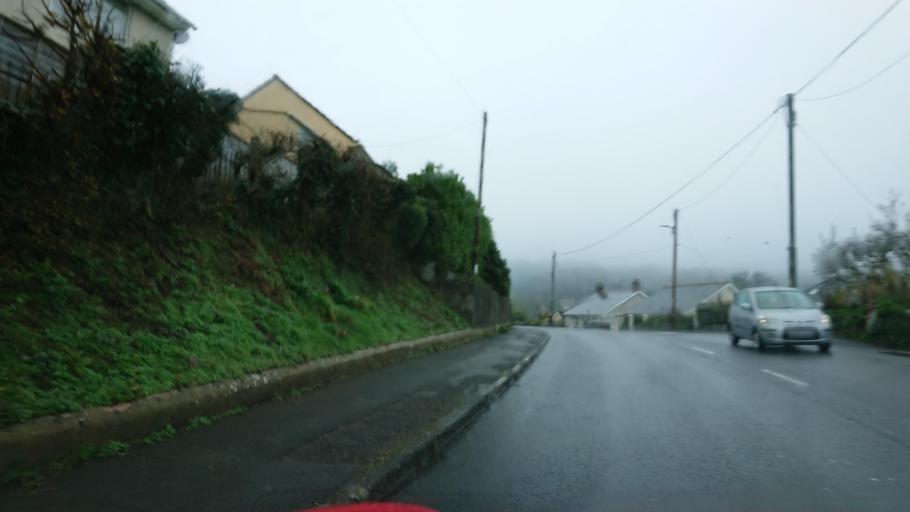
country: GB
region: England
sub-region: Plymouth
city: Plymstock
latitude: 50.3552
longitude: -4.0995
